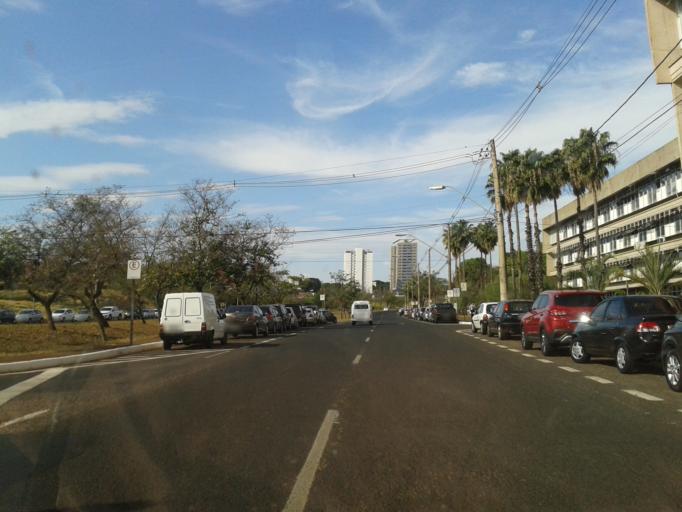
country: BR
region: Minas Gerais
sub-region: Uberlandia
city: Uberlandia
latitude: -18.9119
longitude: -48.2568
